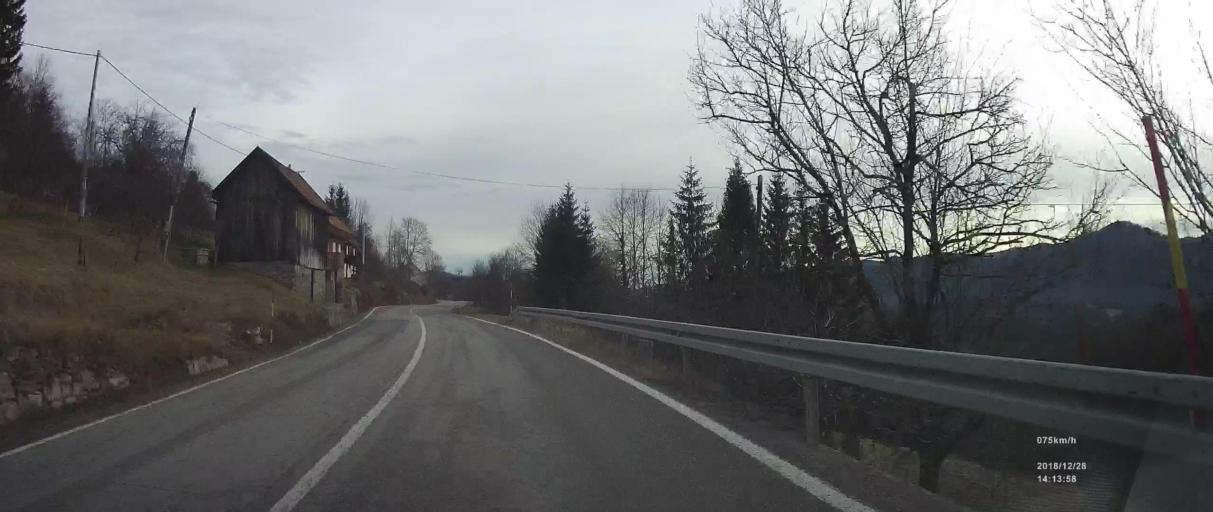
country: HR
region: Primorsko-Goranska
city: Vrbovsko
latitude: 45.4347
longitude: 15.0134
